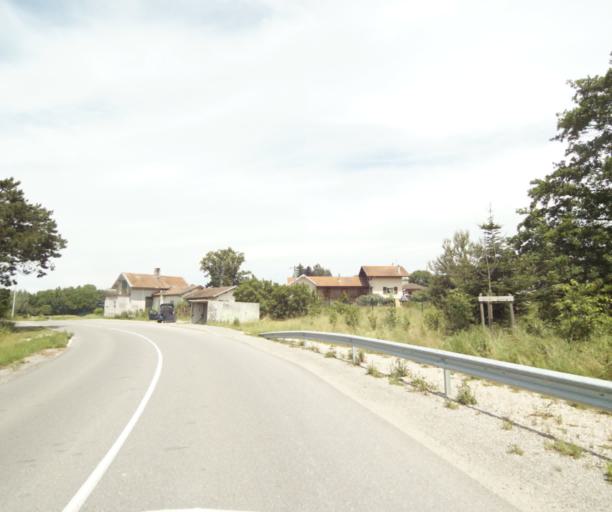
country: FR
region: Rhone-Alpes
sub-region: Departement de la Haute-Savoie
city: Margencel
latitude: 46.3262
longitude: 6.4376
